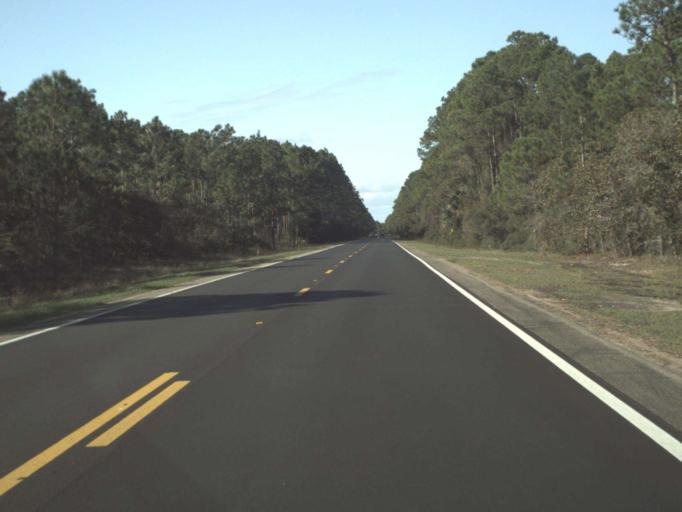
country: US
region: Florida
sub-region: Gulf County
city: Port Saint Joe
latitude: 29.7612
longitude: -85.2590
